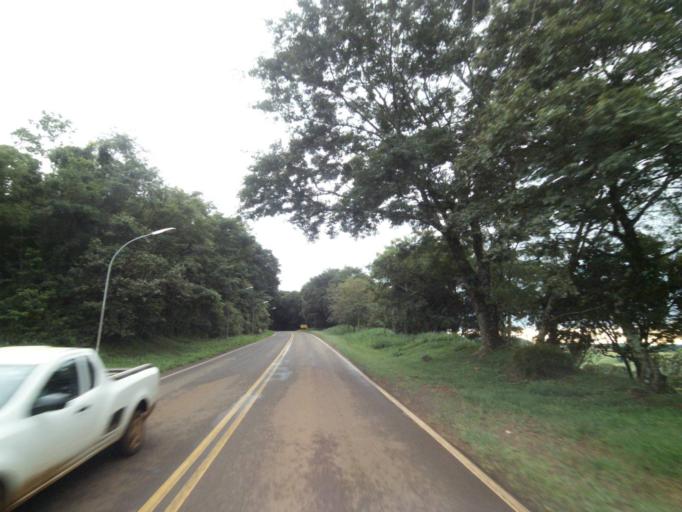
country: BR
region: Parana
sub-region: Guaraniacu
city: Guaraniacu
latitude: -25.1000
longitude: -52.8934
